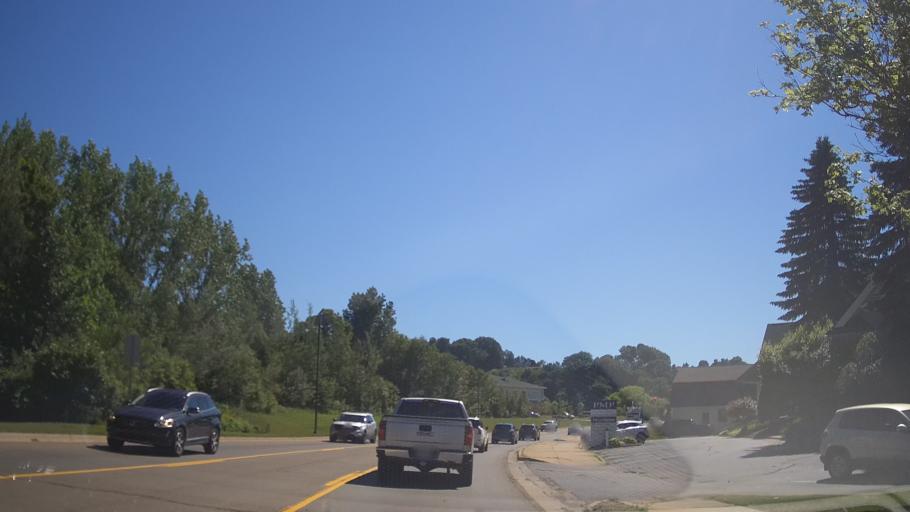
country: US
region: Michigan
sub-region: Emmet County
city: Petoskey
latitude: 45.3826
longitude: -84.9423
